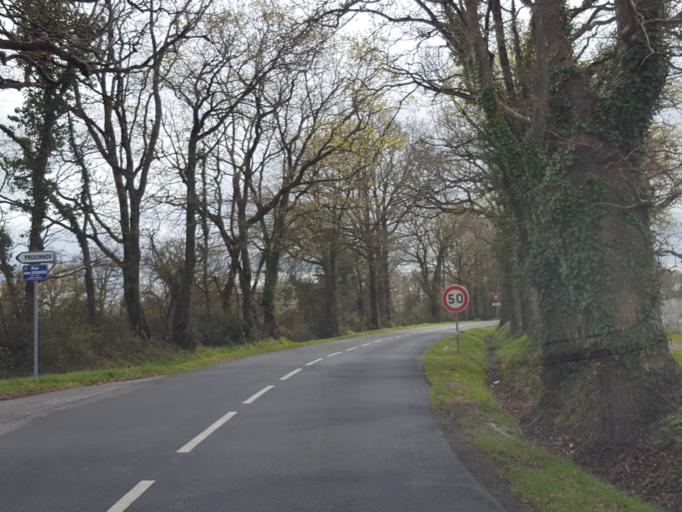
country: FR
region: Pays de la Loire
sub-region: Departement de la Vendee
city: La Roche-sur-Yon
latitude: 46.6724
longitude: -1.3981
